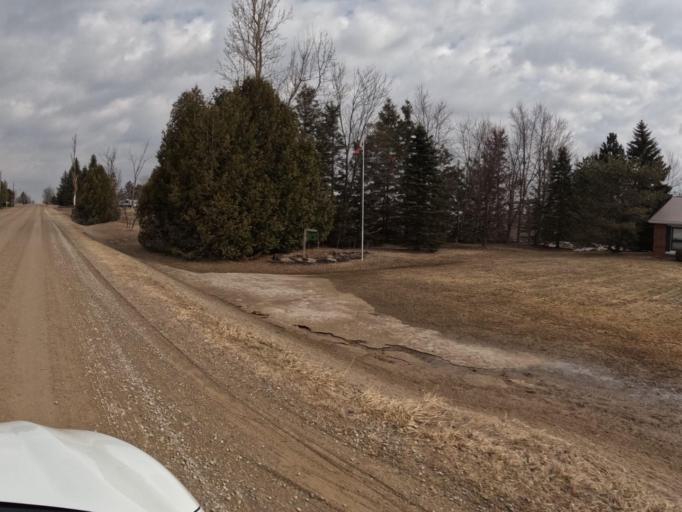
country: CA
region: Ontario
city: Orangeville
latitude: 43.9385
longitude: -80.1898
